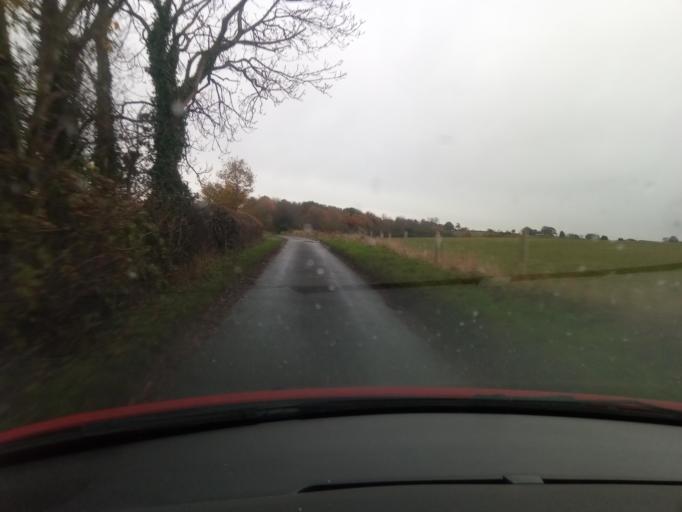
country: GB
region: England
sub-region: Derbyshire
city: Borrowash
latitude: 52.8683
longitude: -1.4103
